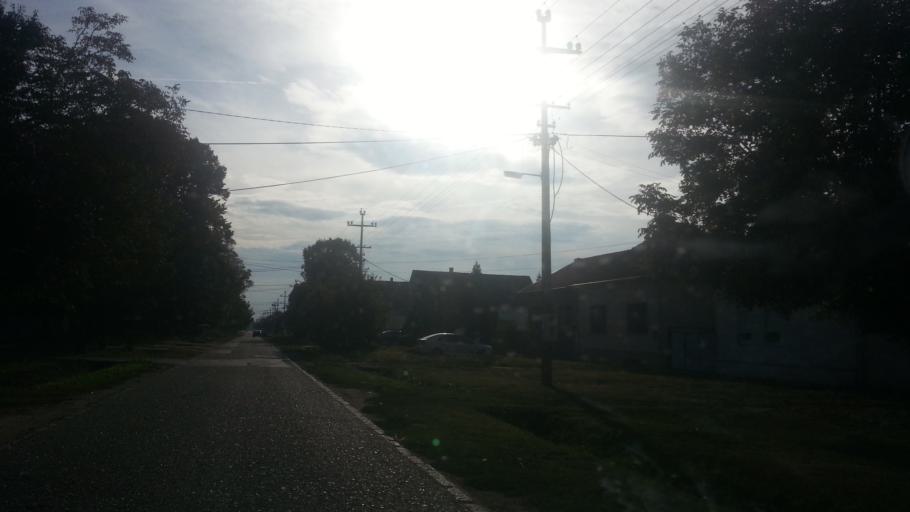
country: RS
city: Belegis
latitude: 45.0230
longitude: 20.3389
